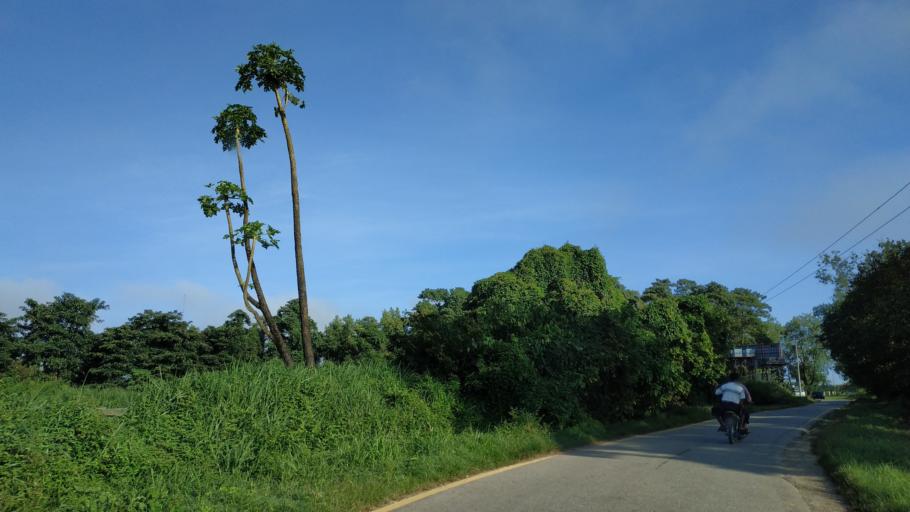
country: MM
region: Tanintharyi
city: Dawei
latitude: 14.0981
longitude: 98.2029
